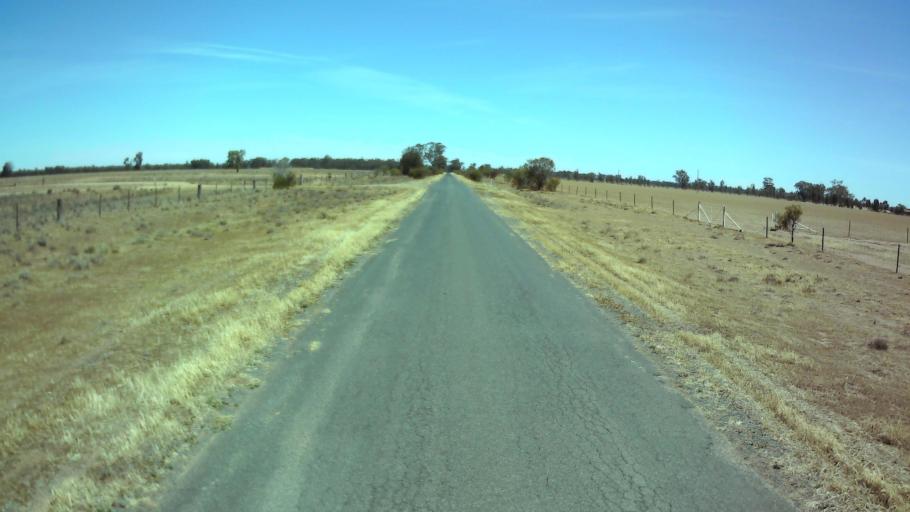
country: AU
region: New South Wales
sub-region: Weddin
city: Grenfell
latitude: -33.8913
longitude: 147.6881
